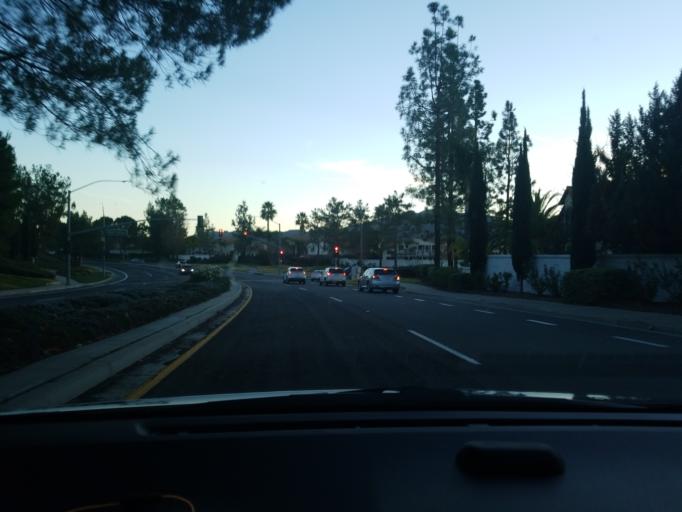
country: US
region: California
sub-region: Riverside County
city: Temecula
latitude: 33.4686
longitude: -117.0959
